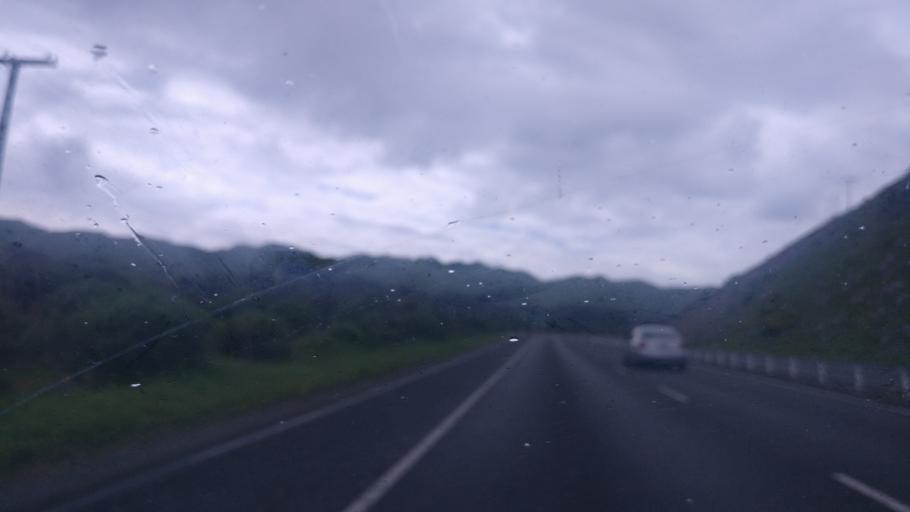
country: NZ
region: Wellington
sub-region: Porirua City
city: Porirua
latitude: -41.0631
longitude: 174.8769
